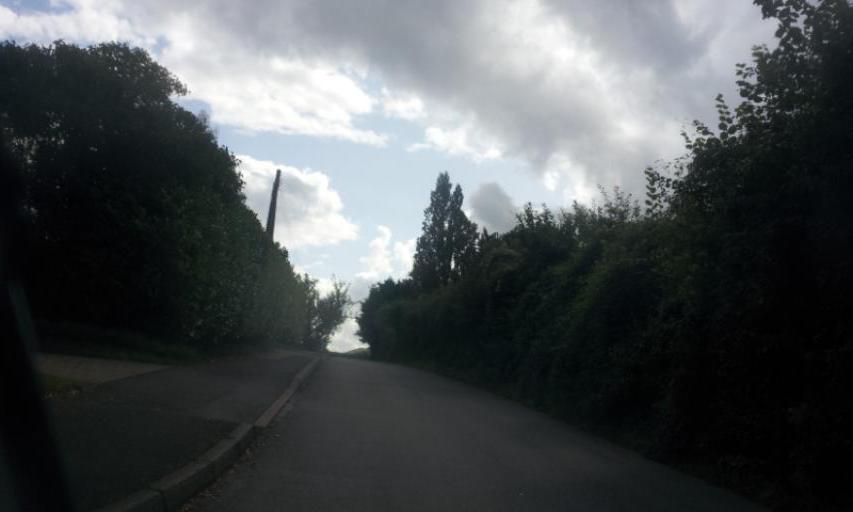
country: GB
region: England
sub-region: Kent
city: Newington
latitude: 51.3449
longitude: 0.6425
